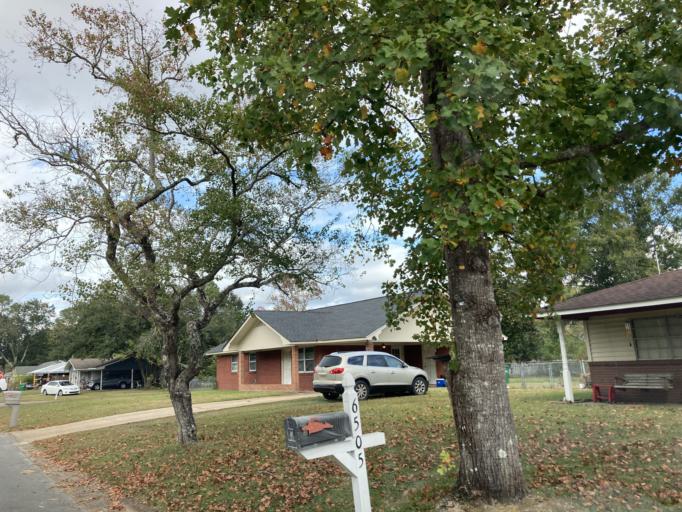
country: US
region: Mississippi
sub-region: Jackson County
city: Gulf Hills
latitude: 30.4356
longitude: -88.8236
